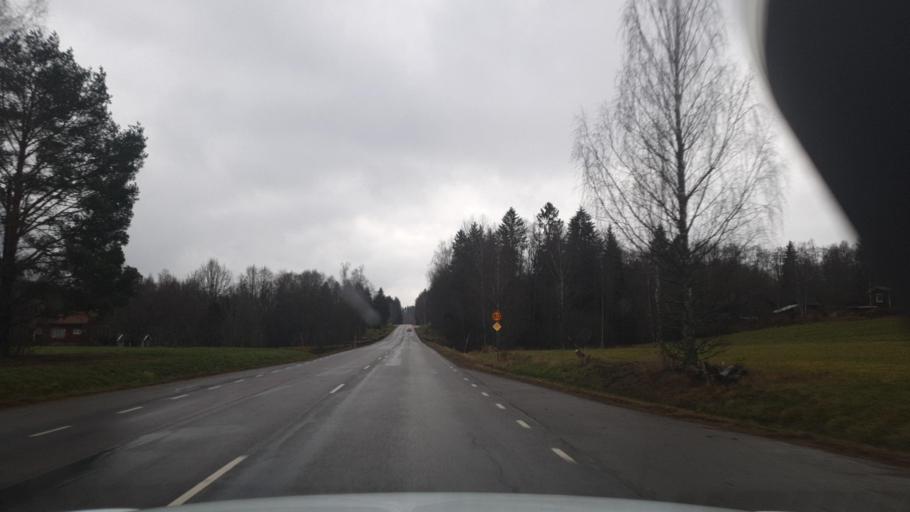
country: SE
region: Vaermland
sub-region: Arvika Kommun
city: Arvika
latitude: 59.6835
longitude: 12.6315
